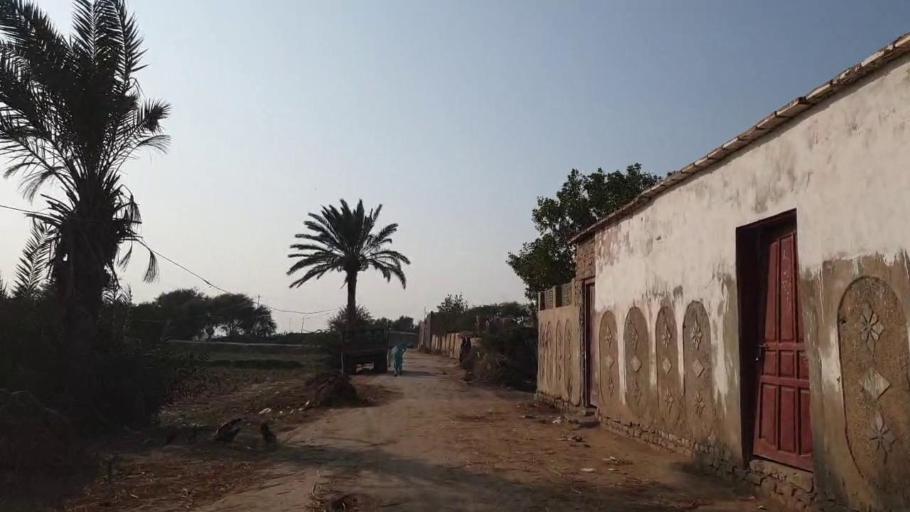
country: PK
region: Sindh
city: Bulri
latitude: 24.9990
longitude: 68.3787
